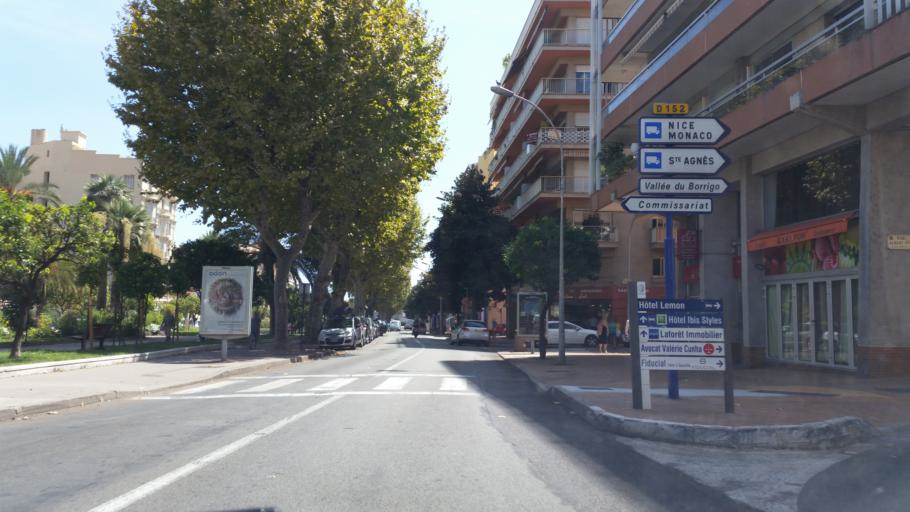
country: FR
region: Provence-Alpes-Cote d'Azur
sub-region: Departement des Alpes-Maritimes
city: Menton
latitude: 43.7754
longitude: 7.4953
